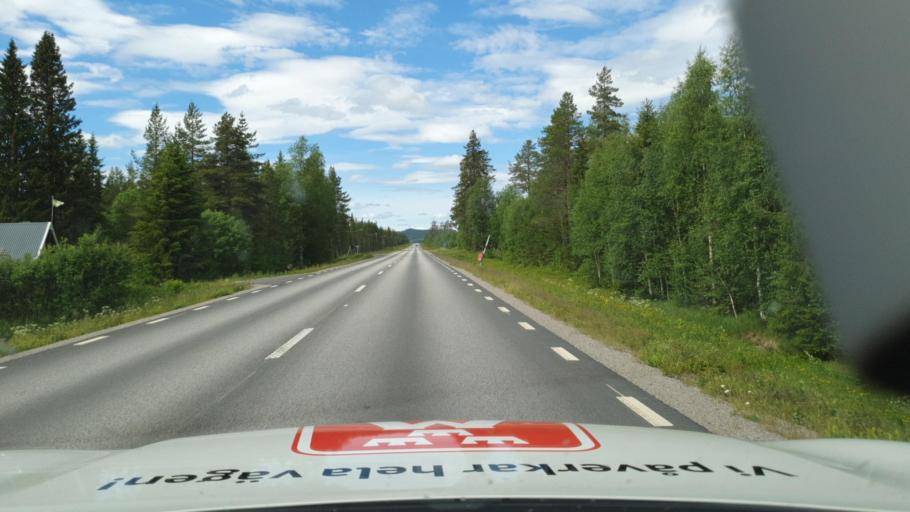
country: SE
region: Vaesterbotten
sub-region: Norsjo Kommun
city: Norsjoe
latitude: 65.2373
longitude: 19.7221
